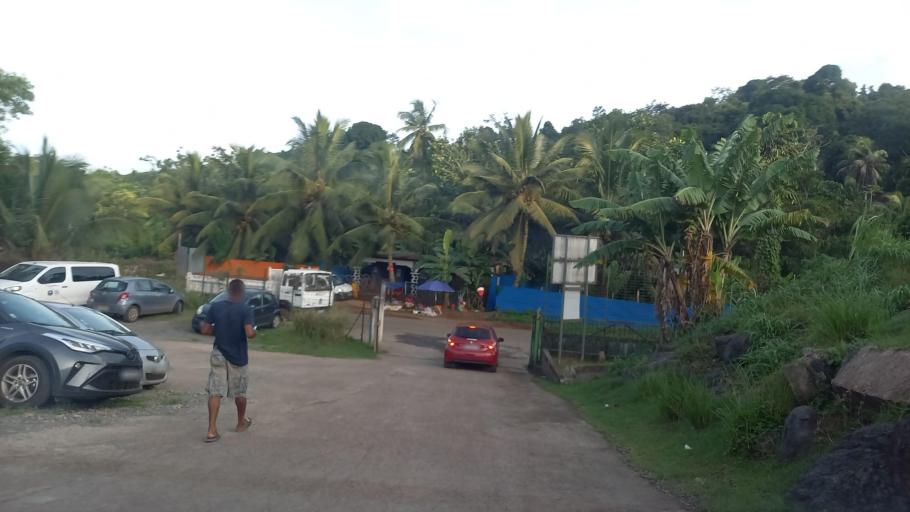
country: YT
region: Bandraboua
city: Bandraboua
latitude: -12.7269
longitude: 45.1208
